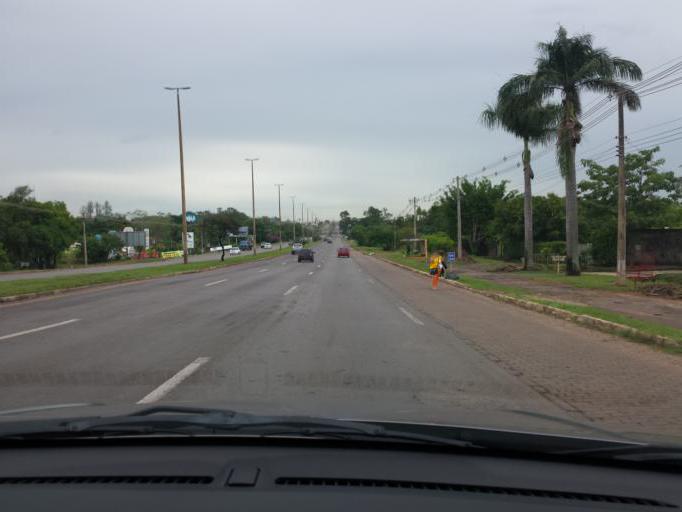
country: BR
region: Federal District
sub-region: Brasilia
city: Brasilia
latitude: -15.8704
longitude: -47.9580
